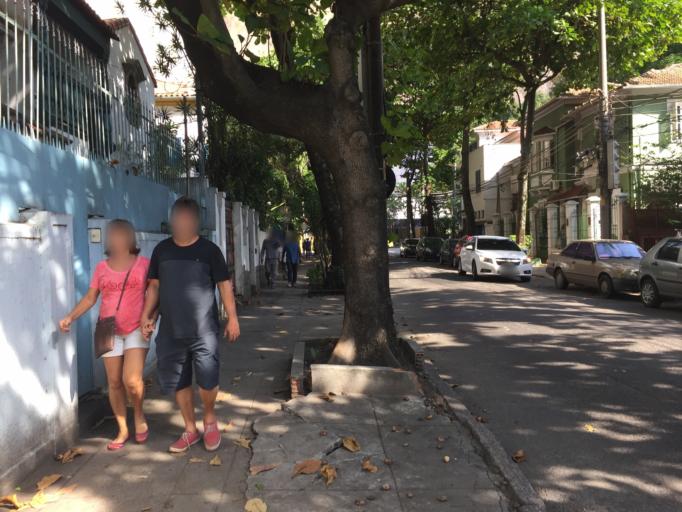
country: BR
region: Rio de Janeiro
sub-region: Rio De Janeiro
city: Rio de Janeiro
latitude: -22.9538
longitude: -43.1673
